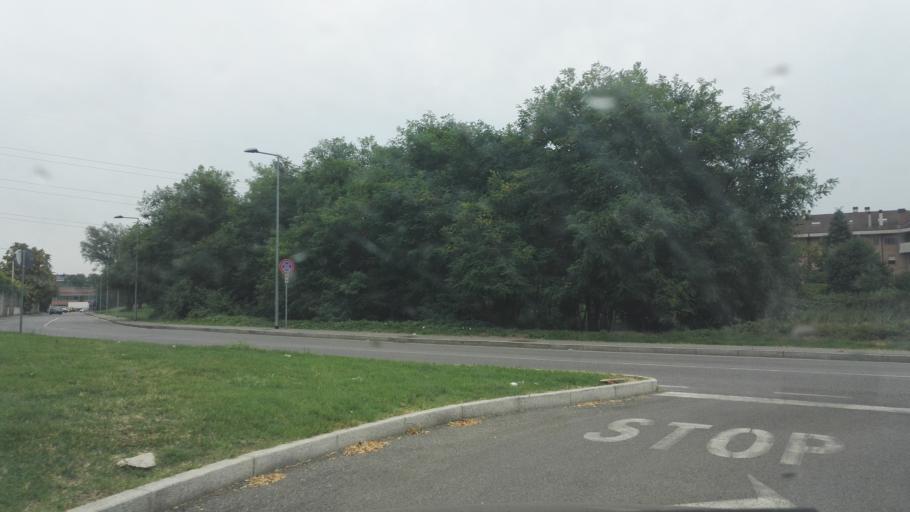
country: IT
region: Lombardy
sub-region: Citta metropolitana di Milano
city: Bettola-Zeloforomagno
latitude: 45.4250
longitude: 9.3039
